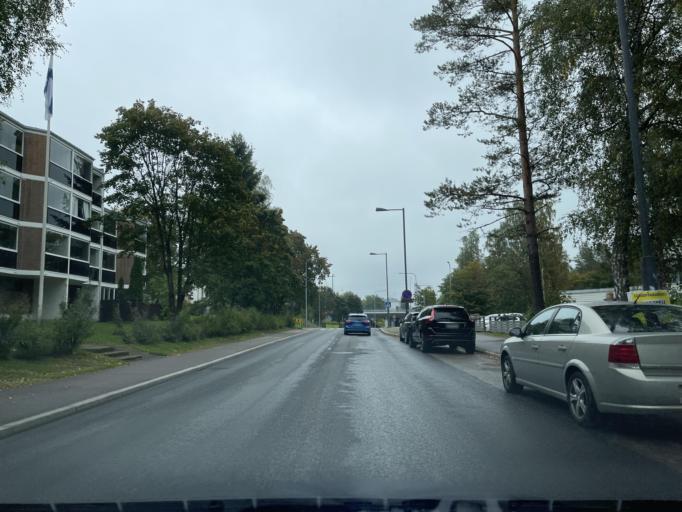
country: FI
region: Uusimaa
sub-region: Helsinki
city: Hyvinge
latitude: 60.6270
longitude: 24.8606
